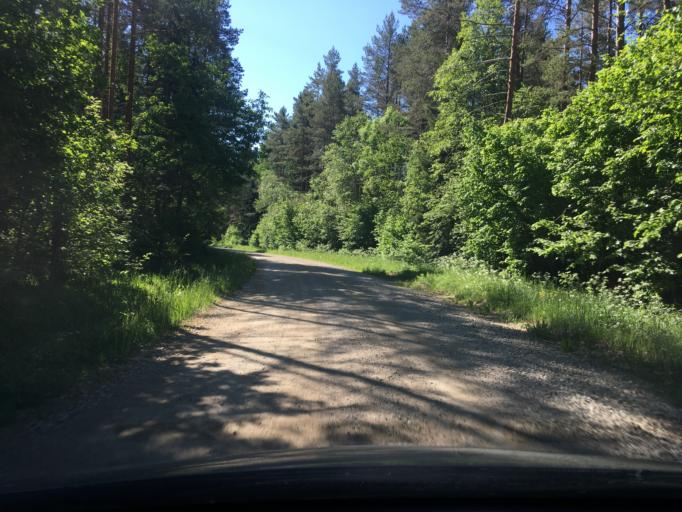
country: EE
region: Laeaene
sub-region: Lihula vald
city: Lihula
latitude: 58.6388
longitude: 23.7915
